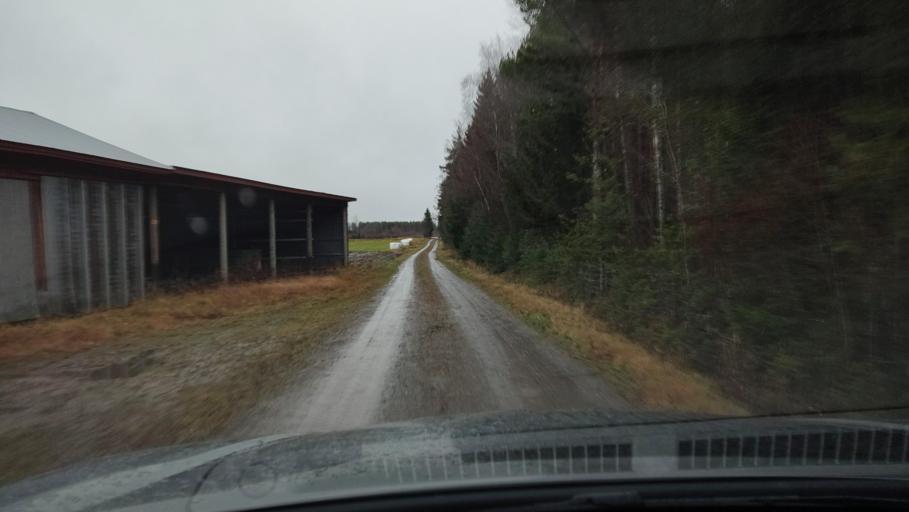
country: FI
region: Southern Ostrobothnia
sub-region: Suupohja
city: Karijoki
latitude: 62.2303
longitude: 21.5516
